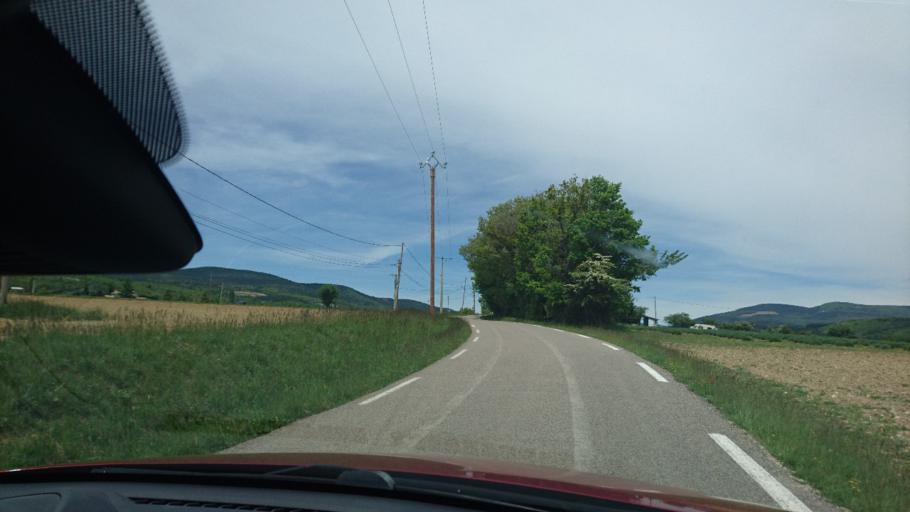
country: FR
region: Provence-Alpes-Cote d'Azur
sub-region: Departement du Vaucluse
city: Sault
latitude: 44.1068
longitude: 5.4005
